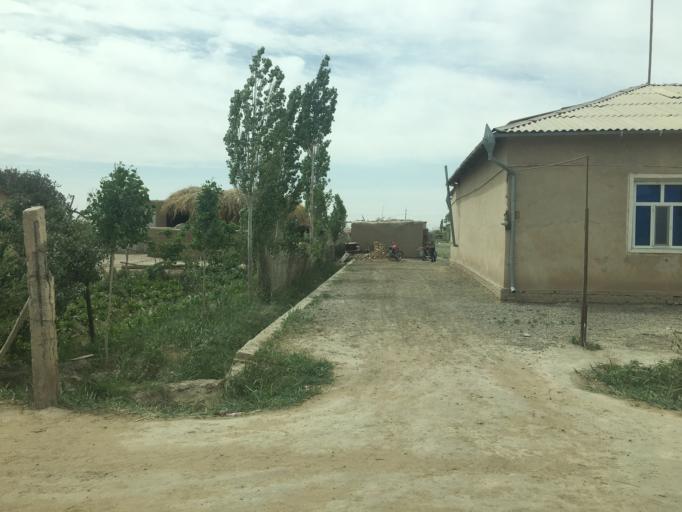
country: TM
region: Dasoguz
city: Tagta
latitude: 41.6130
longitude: 59.8239
